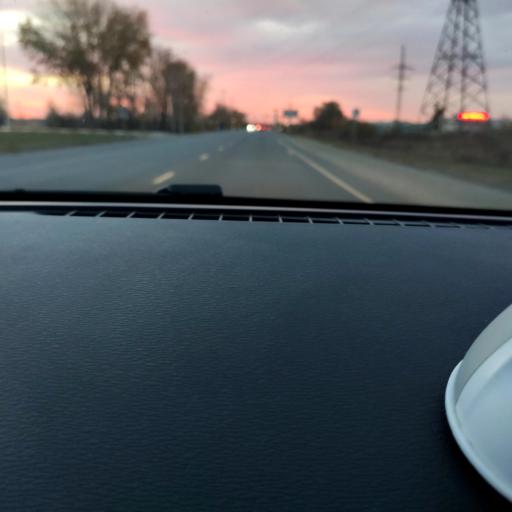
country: RU
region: Samara
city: Samara
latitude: 53.1293
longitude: 50.1553
